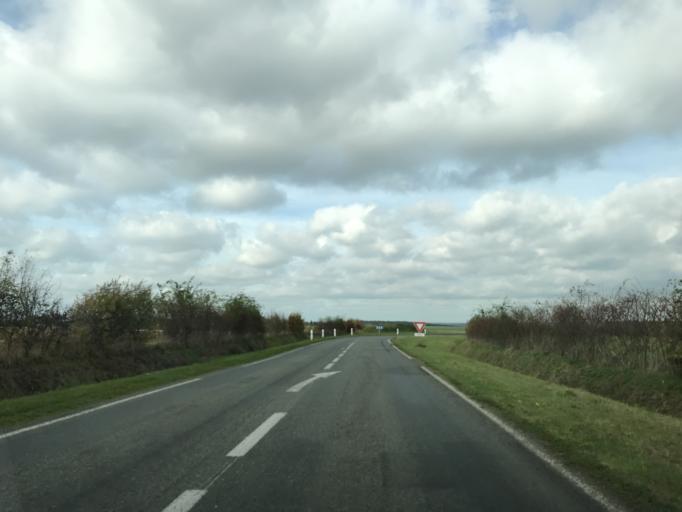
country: FR
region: Haute-Normandie
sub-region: Departement de l'Eure
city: Fleury-sur-Andelle
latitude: 49.3363
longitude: 1.3796
